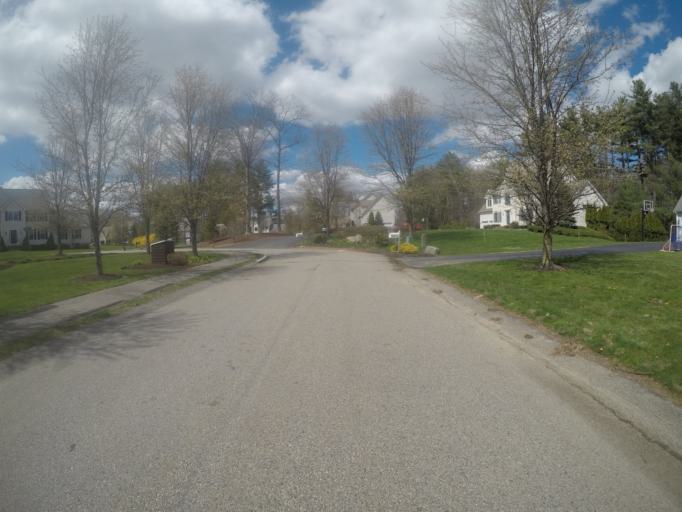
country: US
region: Massachusetts
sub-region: Bristol County
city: Easton
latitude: 42.0202
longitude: -71.0684
